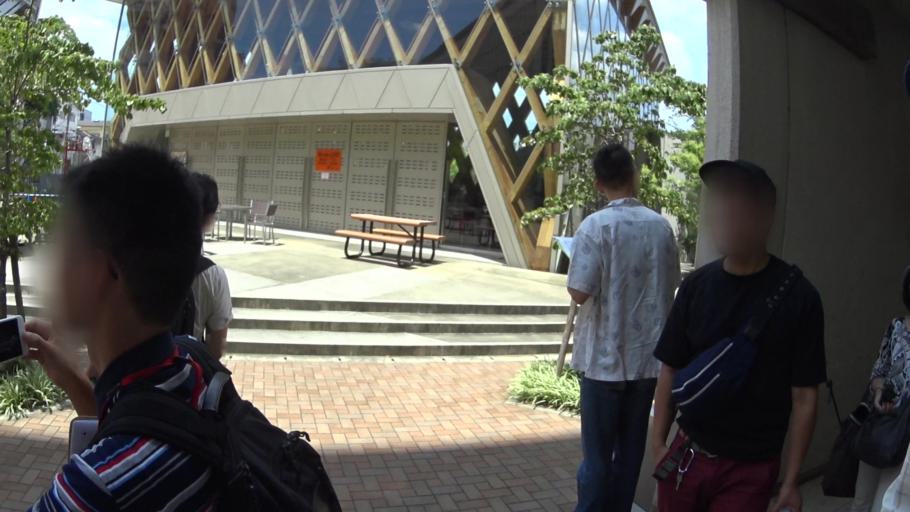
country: JP
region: Osaka
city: Yao
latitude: 34.6521
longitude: 135.5865
